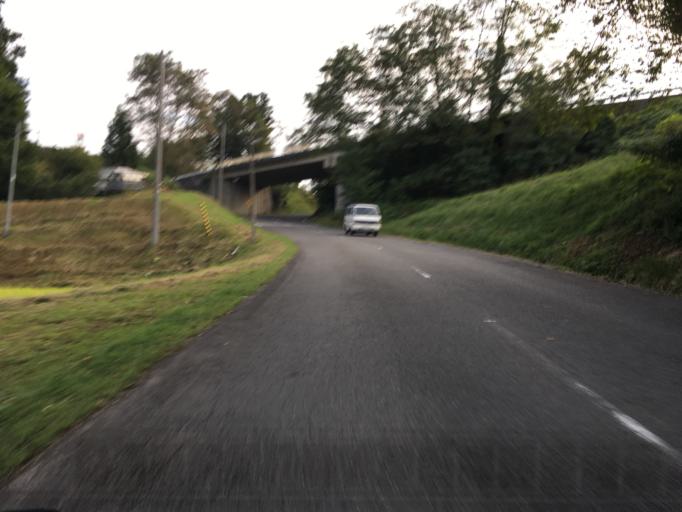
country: JP
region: Fukushima
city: Fukushima-shi
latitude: 37.6869
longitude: 140.5488
